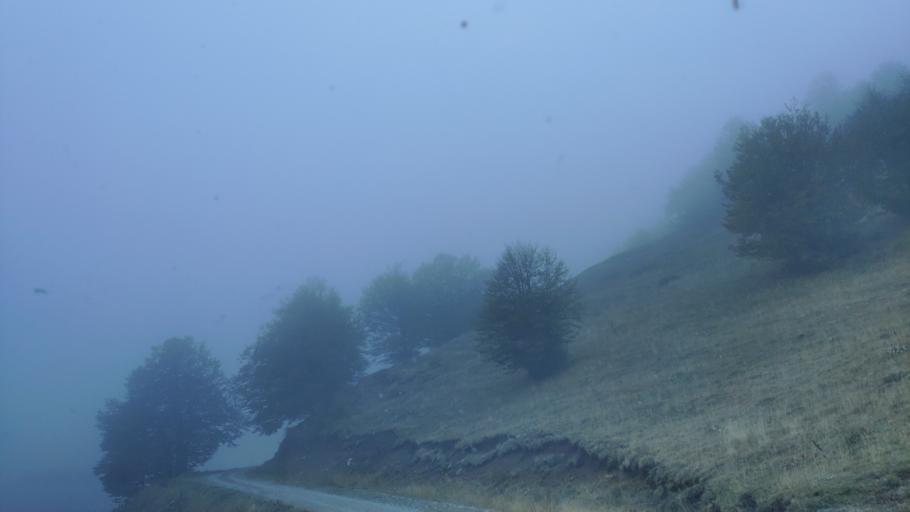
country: GR
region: West Macedonia
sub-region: Nomos Kastorias
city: Nestorio
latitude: 40.2999
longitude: 20.9199
